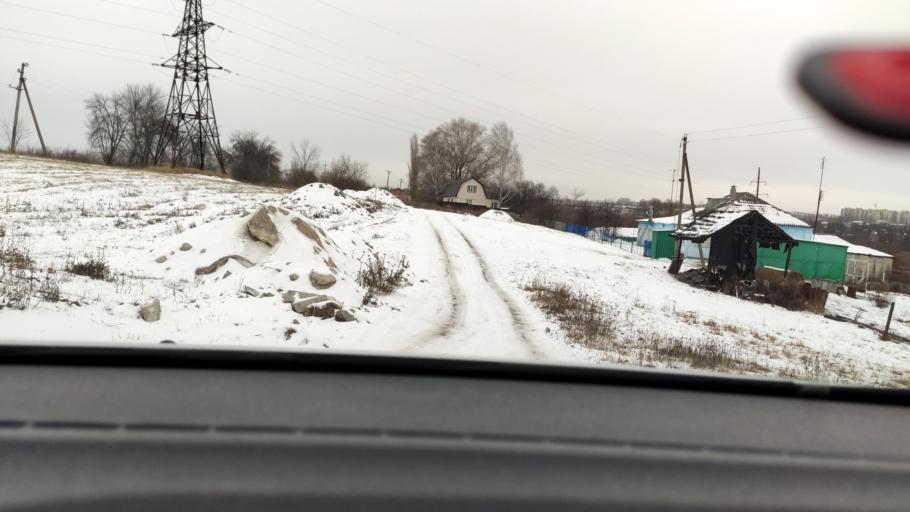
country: RU
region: Voronezj
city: Semiluki
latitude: 51.7029
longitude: 38.9819
